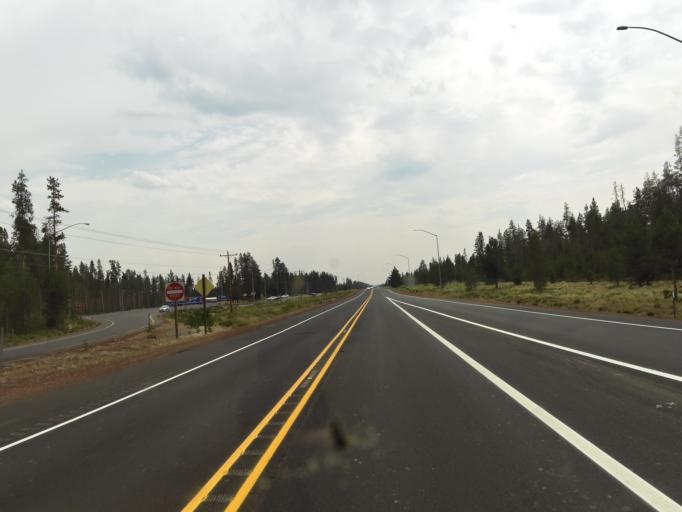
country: US
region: Oregon
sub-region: Deschutes County
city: La Pine
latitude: 43.1744
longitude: -121.7862
